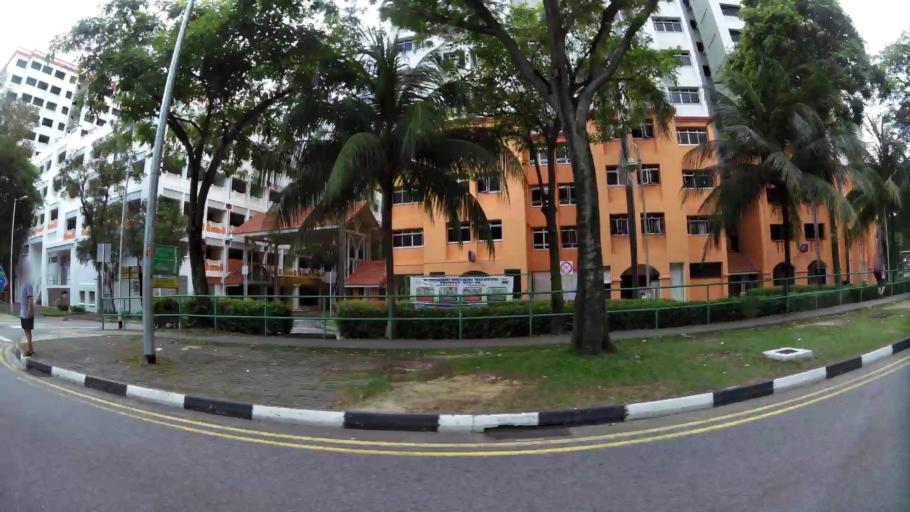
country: MY
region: Johor
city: Johor Bahru
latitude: 1.4524
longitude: 103.8169
